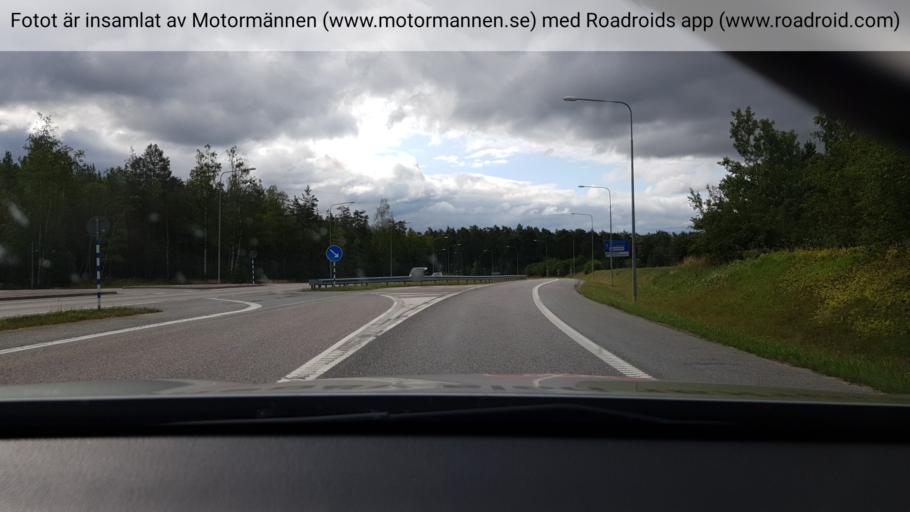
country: SE
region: Stockholm
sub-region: Nacka Kommun
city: Alta
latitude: 59.2422
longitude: 18.1847
